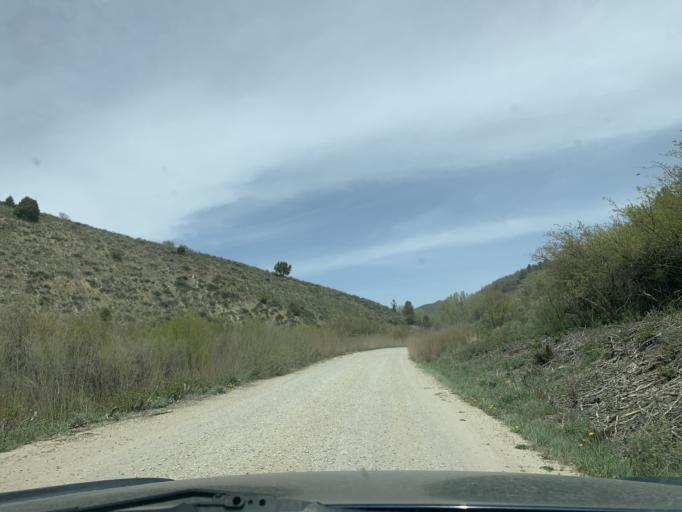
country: US
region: Utah
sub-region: Utah County
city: Mapleton
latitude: 40.1678
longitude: -111.3306
